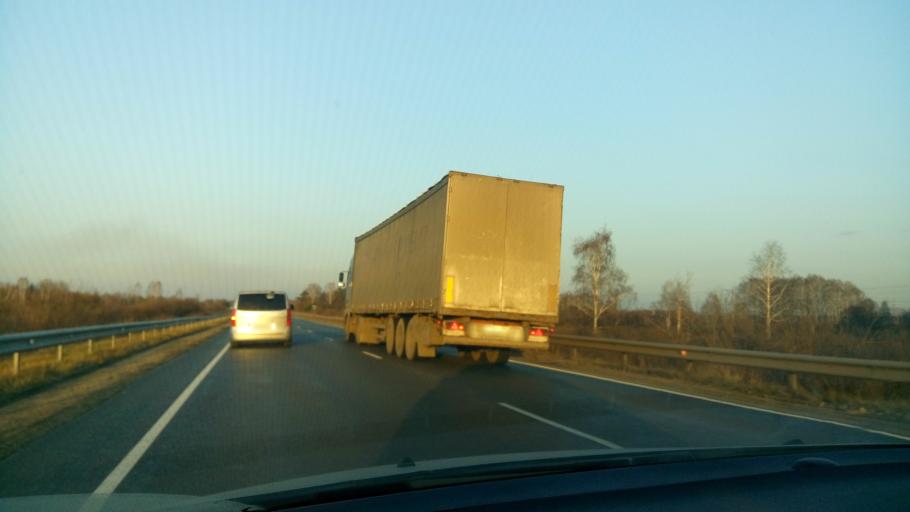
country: RU
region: Sverdlovsk
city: Yelanskiy
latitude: 56.8178
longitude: 62.5422
